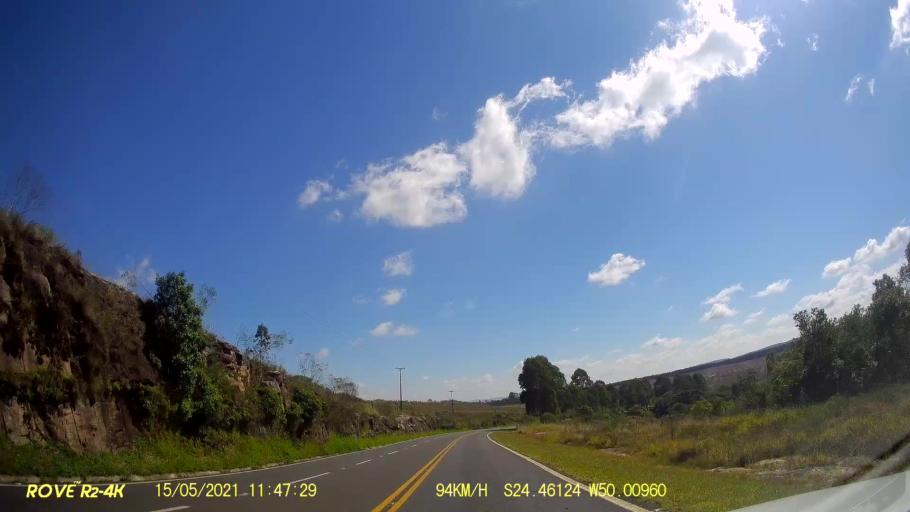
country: BR
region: Parana
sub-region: Pirai Do Sul
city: Pirai do Sul
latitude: -24.4612
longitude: -50.0097
